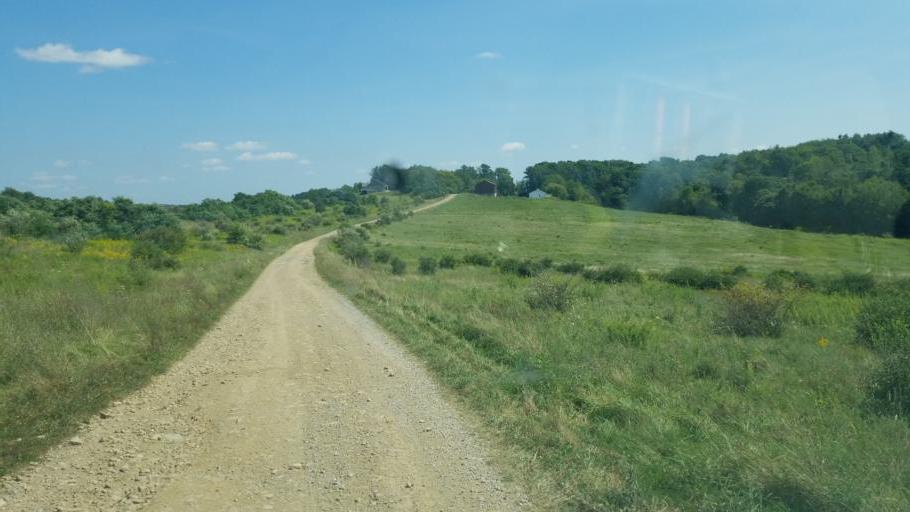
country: US
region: Pennsylvania
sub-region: Clarion County
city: Knox
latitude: 41.1026
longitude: -79.5285
